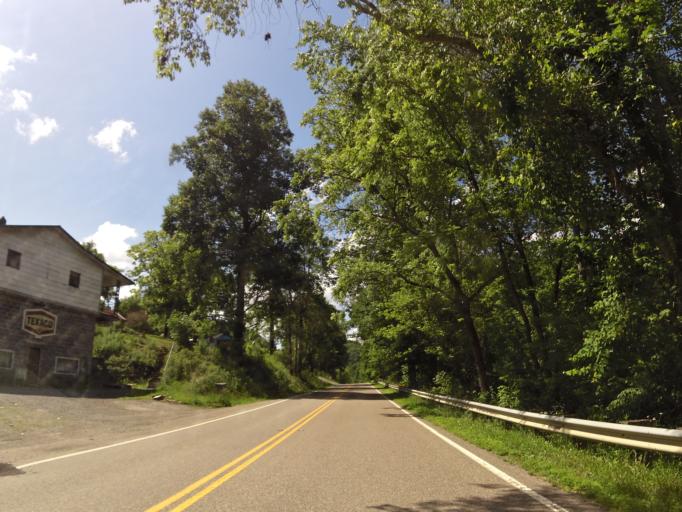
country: US
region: Virginia
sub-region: Lee County
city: Pennington Gap
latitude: 36.7650
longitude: -83.0945
